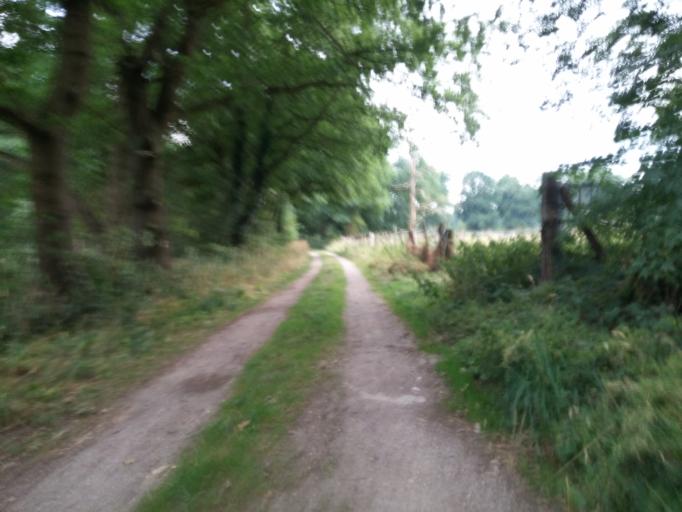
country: DE
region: North Rhine-Westphalia
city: Tonisvorst
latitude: 51.3915
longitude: 6.5268
